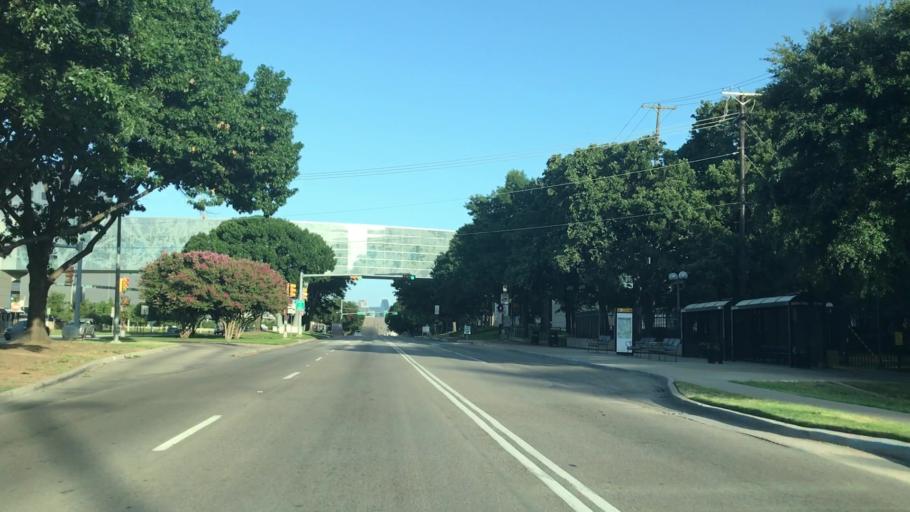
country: US
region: Texas
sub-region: Dallas County
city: Dallas
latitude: 32.8127
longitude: -96.8386
